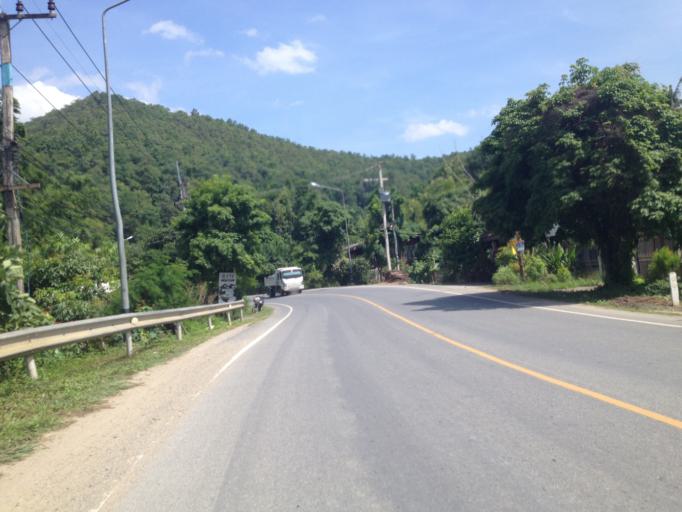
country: TH
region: Chiang Mai
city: Hang Dong
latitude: 18.7339
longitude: 98.9048
